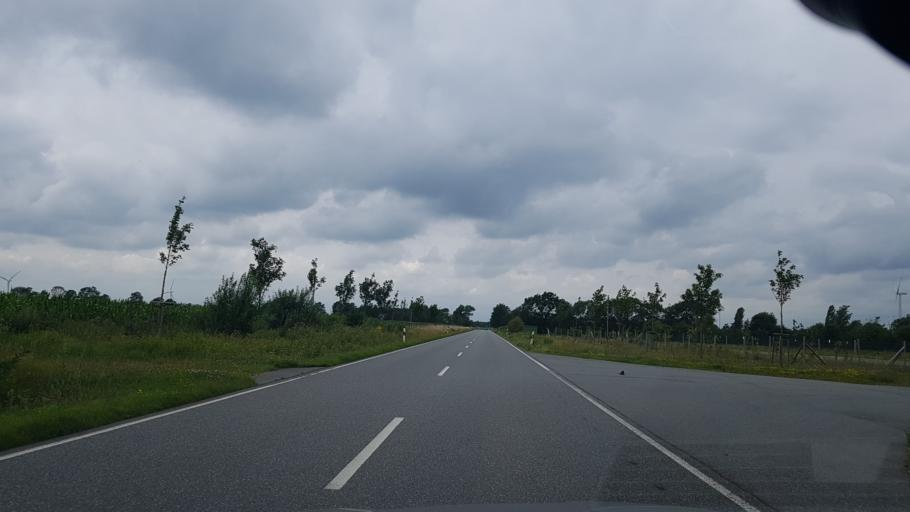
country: DE
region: Schleswig-Holstein
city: Boxlund
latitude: 54.8493
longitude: 9.1961
